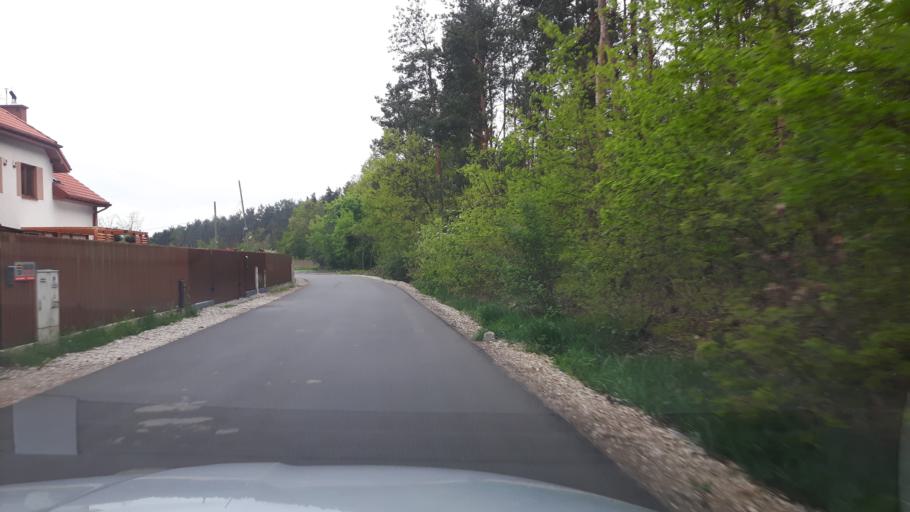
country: PL
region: Masovian Voivodeship
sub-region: Warszawa
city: Rembertow
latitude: 52.2776
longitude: 21.1472
